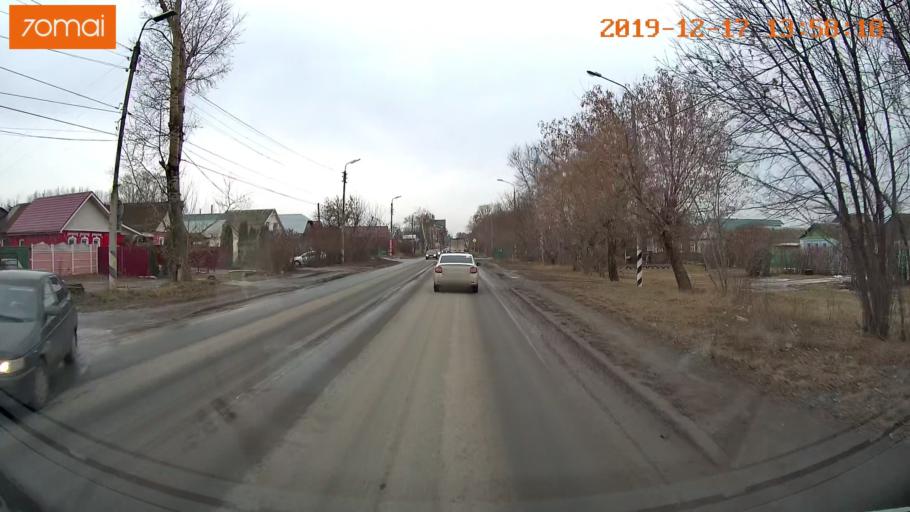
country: RU
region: Rjazan
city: Ryazan'
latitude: 54.6236
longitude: 39.6851
